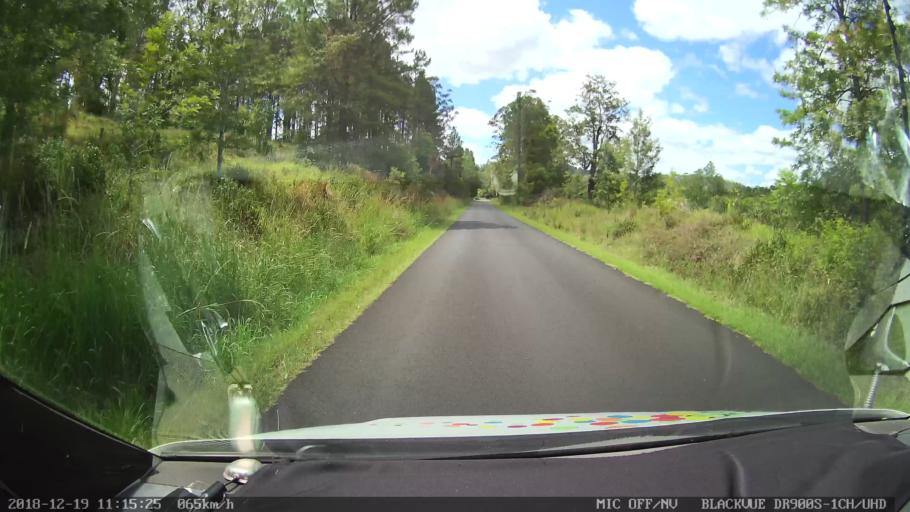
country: AU
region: New South Wales
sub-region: Lismore Municipality
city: Nimbin
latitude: -28.6677
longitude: 153.2779
